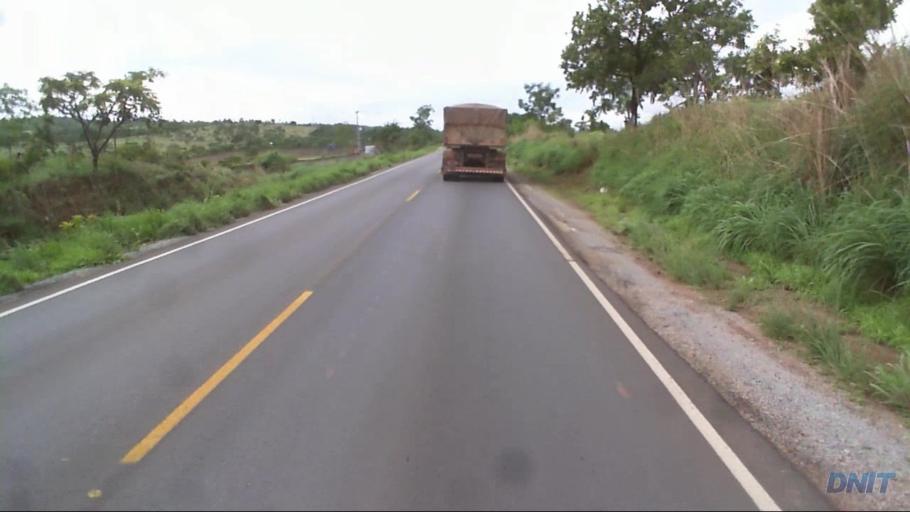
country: BR
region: Goias
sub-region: Padre Bernardo
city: Padre Bernardo
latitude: -15.1919
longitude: -48.2842
